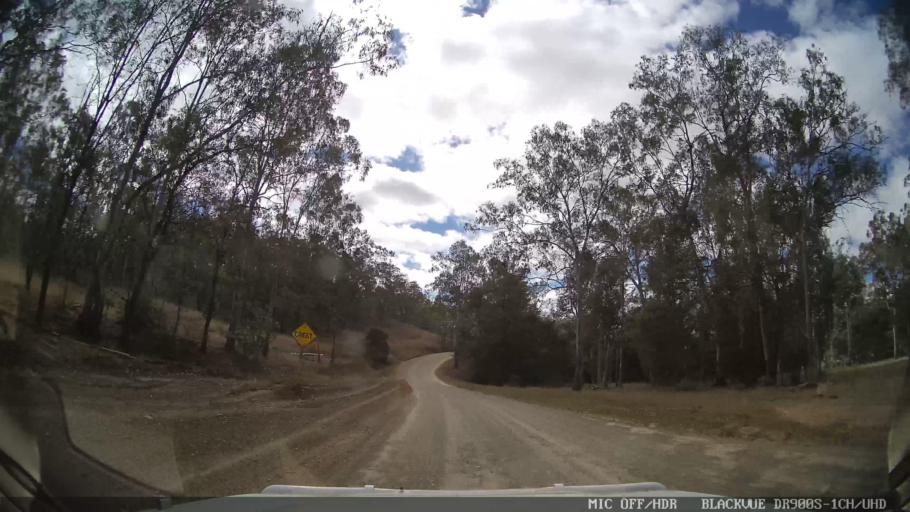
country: AU
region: Queensland
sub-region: Gladstone
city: Toolooa
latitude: -24.5536
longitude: 151.3361
